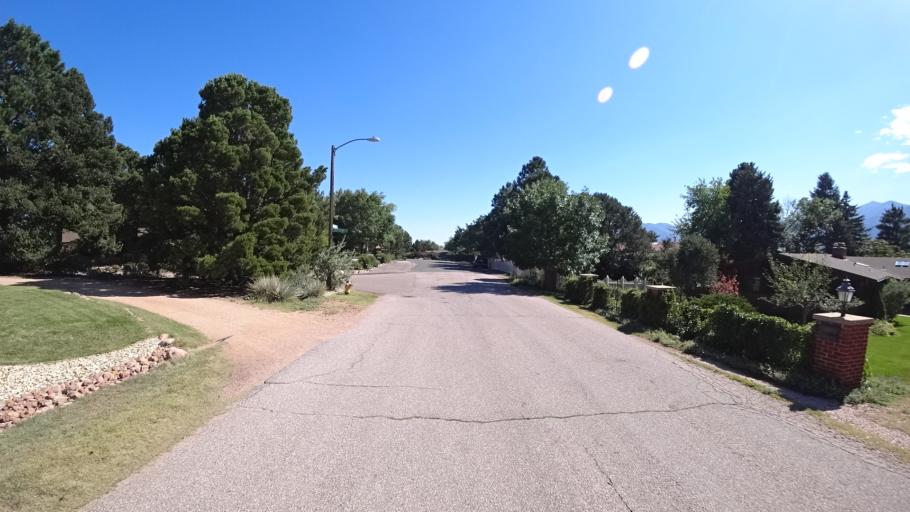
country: US
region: Colorado
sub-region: El Paso County
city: Colorado Springs
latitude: 38.8623
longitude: -104.8582
